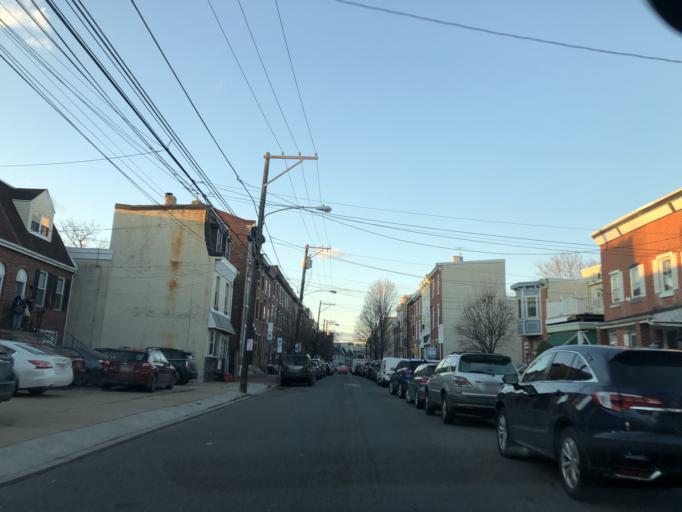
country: US
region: Pennsylvania
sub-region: Philadelphia County
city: Philadelphia
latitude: 39.9716
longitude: -75.1328
